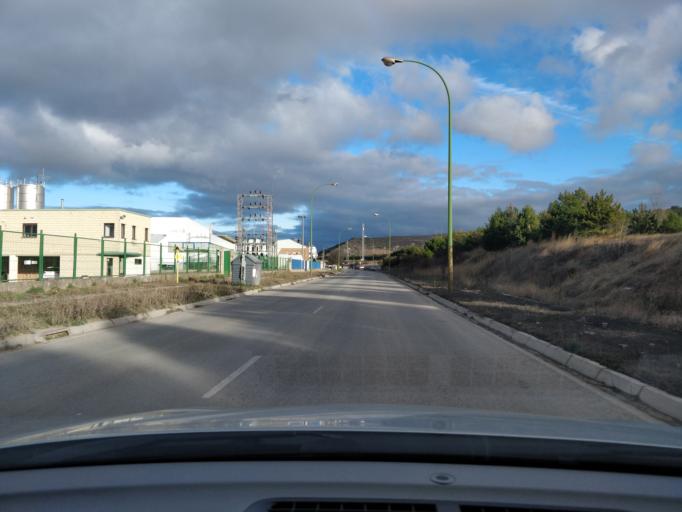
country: ES
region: Castille and Leon
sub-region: Provincia de Burgos
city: Villalbilla de Burgos
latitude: 42.3650
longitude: -3.7412
